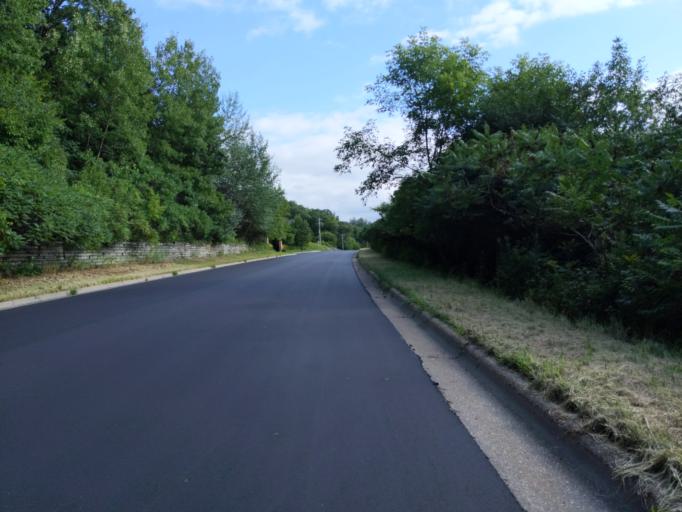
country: US
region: Minnesota
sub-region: Hennepin County
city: Hopkins
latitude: 44.8939
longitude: -93.4331
